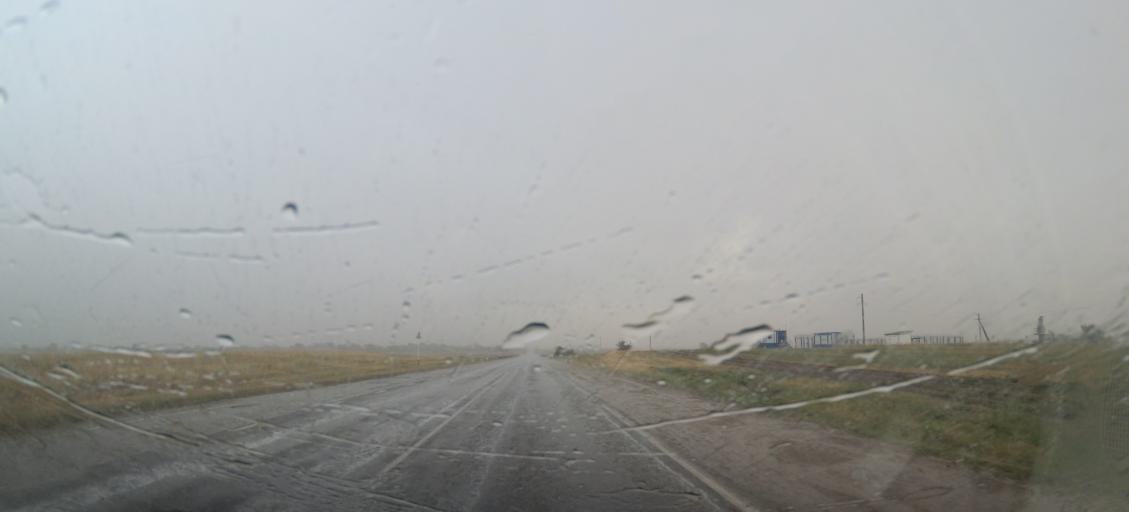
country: RU
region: Rostov
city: Proletarsk
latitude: 46.6780
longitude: 41.7060
